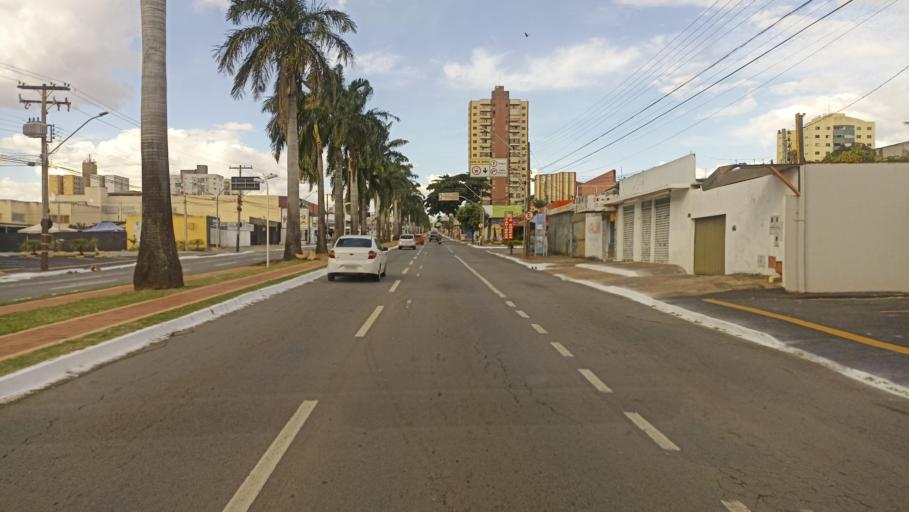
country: BR
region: Goias
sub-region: Goiania
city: Goiania
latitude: -16.7176
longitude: -49.2918
